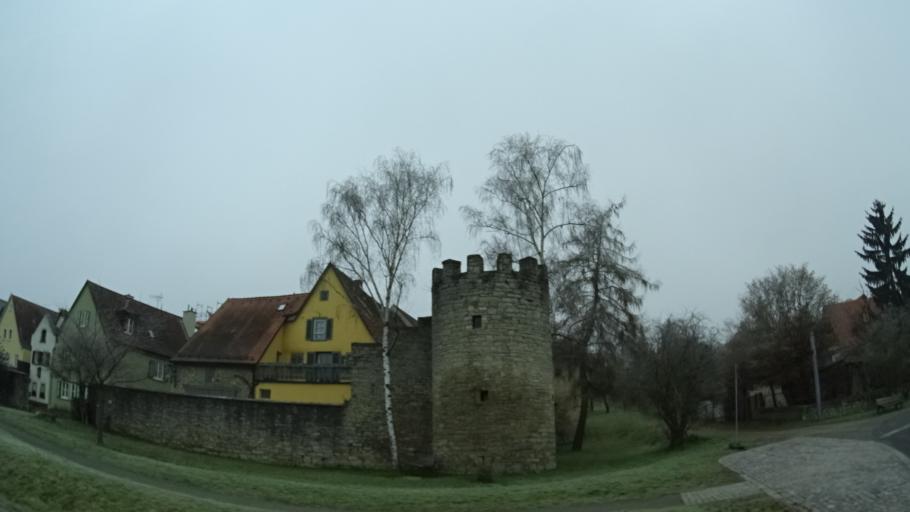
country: DE
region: Bavaria
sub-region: Regierungsbezirk Unterfranken
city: Sulzfeld am Main
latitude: 49.7087
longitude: 10.1346
